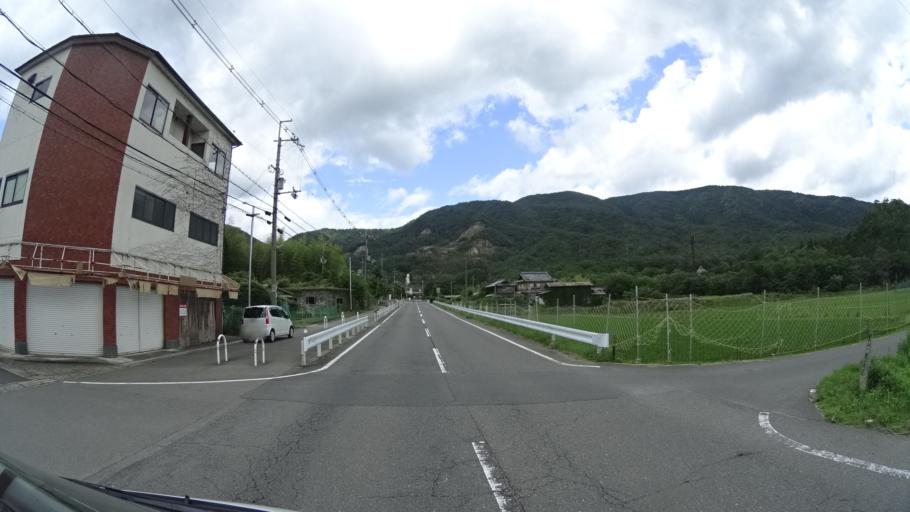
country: JP
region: Kyoto
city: Kameoka
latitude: 35.0119
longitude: 135.4306
